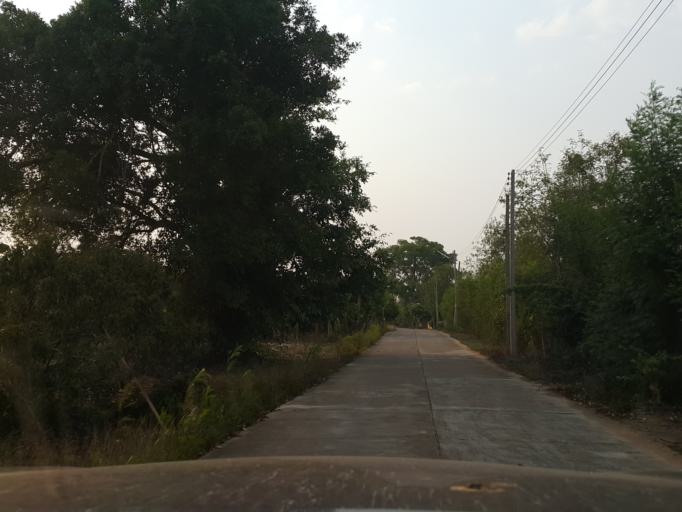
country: TH
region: Lamphun
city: Li
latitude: 17.8078
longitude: 98.9495
